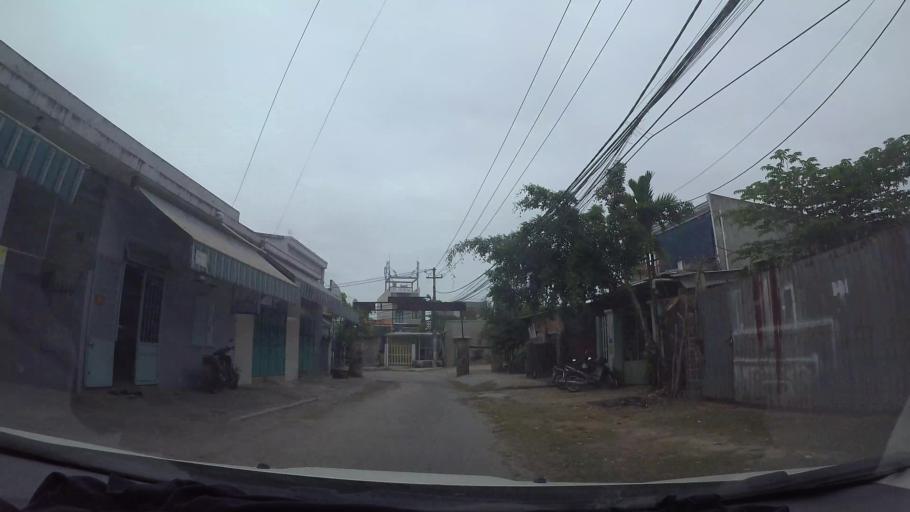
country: VN
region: Da Nang
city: Lien Chieu
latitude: 16.0650
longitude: 108.1483
